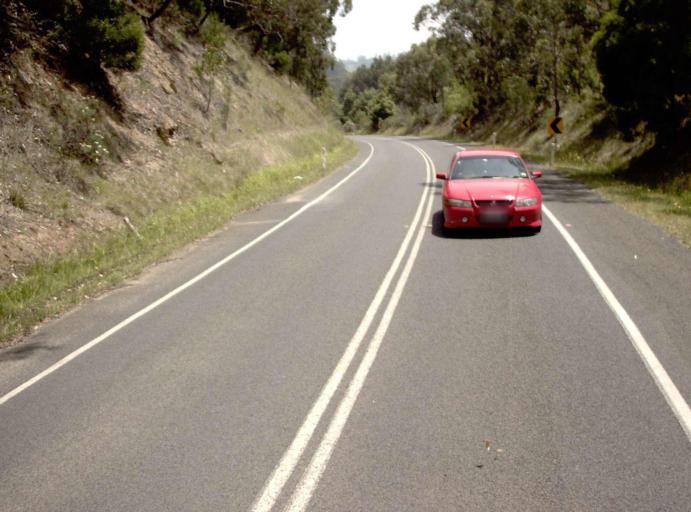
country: AU
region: Victoria
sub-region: Latrobe
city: Traralgon
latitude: -38.3590
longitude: 146.7522
